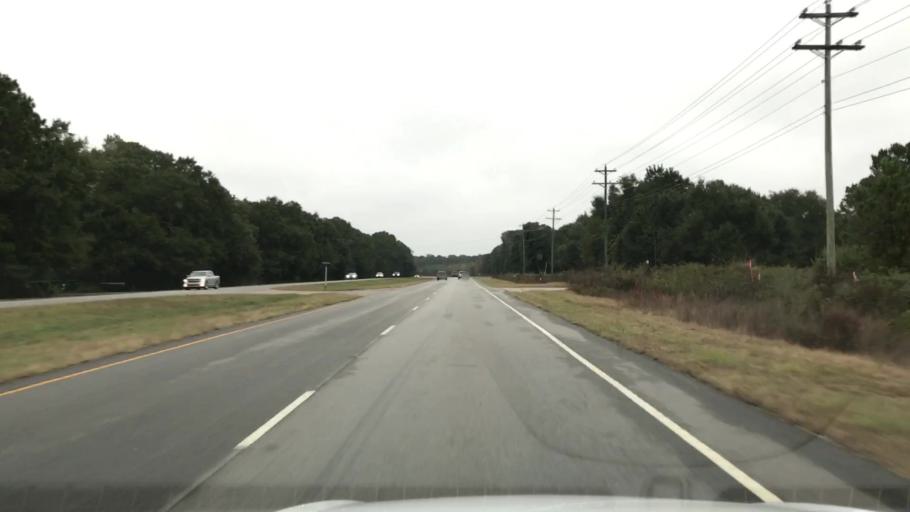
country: US
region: South Carolina
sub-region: Charleston County
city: Isle of Palms
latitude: 32.9137
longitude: -79.7202
